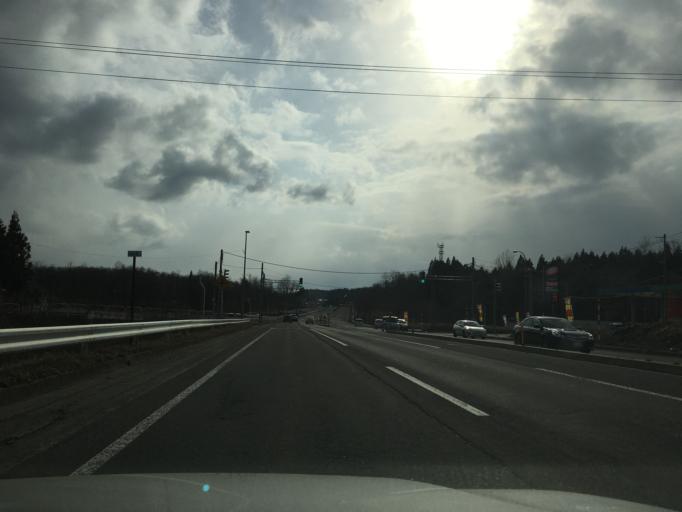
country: JP
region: Aomori
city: Aomori Shi
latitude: 40.8288
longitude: 140.6591
